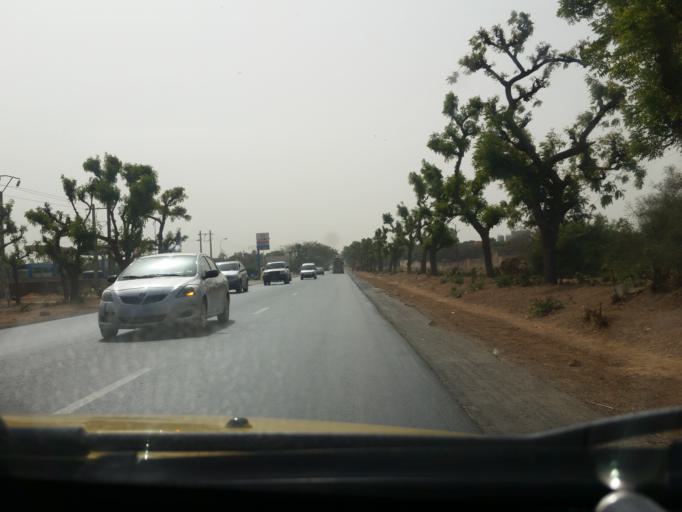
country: SN
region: Thies
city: Thies Nones
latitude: 14.7840
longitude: -16.9712
